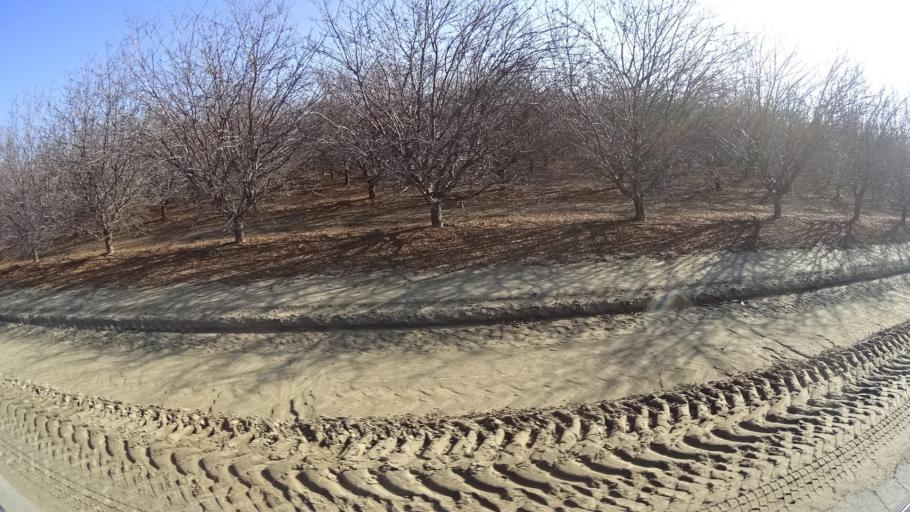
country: US
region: California
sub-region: Kern County
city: Arvin
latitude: 35.1720
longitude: -118.8781
